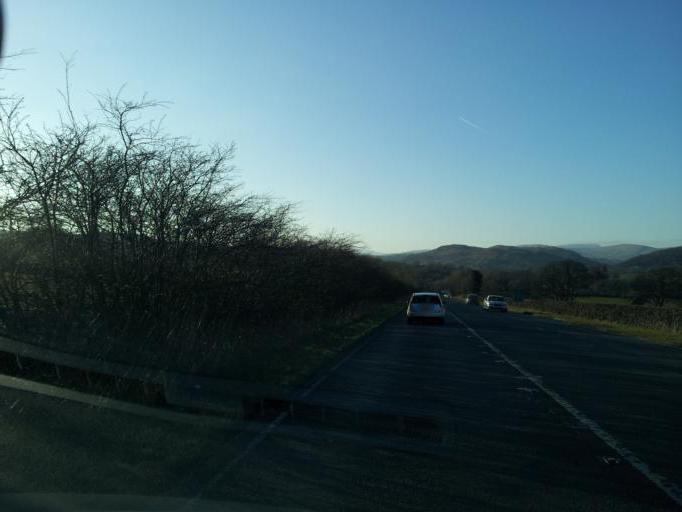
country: GB
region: England
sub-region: Cumbria
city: Kendal
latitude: 54.3596
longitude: -2.7887
